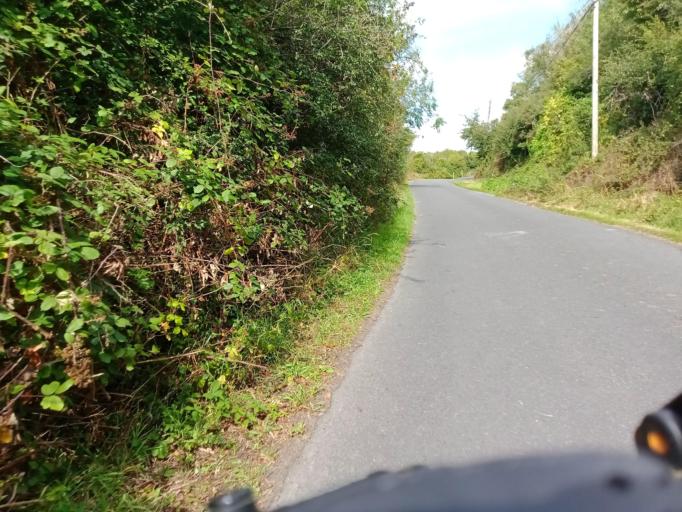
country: IE
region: Munster
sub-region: Waterford
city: Dungarvan
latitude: 52.1113
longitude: -7.5086
